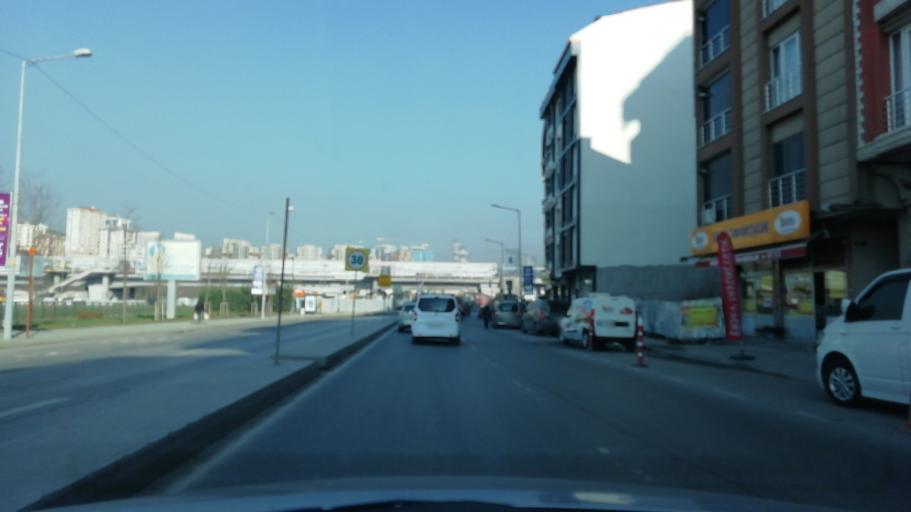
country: TR
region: Istanbul
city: Sisli
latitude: 41.0772
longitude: 28.9501
